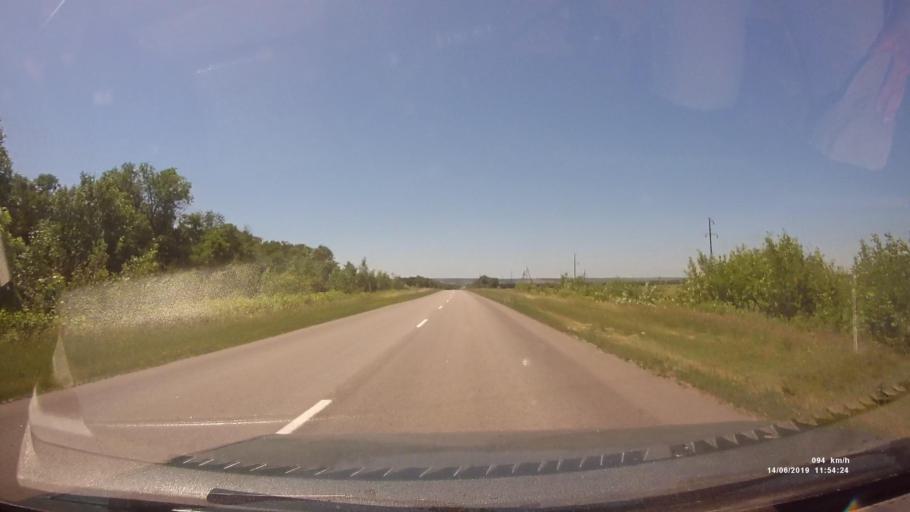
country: RU
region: Rostov
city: Kazanskaya
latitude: 49.8194
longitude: 41.1950
